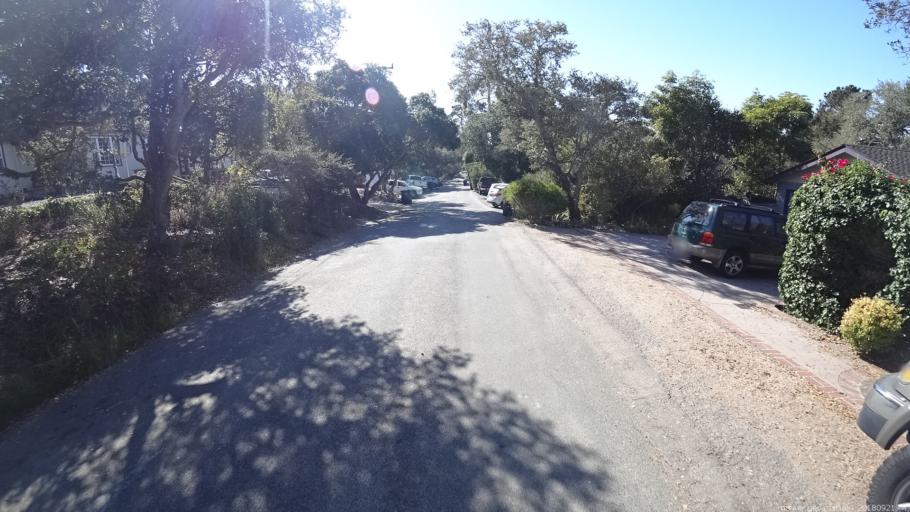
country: US
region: California
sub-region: Monterey County
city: Carmel-by-the-Sea
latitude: 36.5648
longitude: -121.9182
